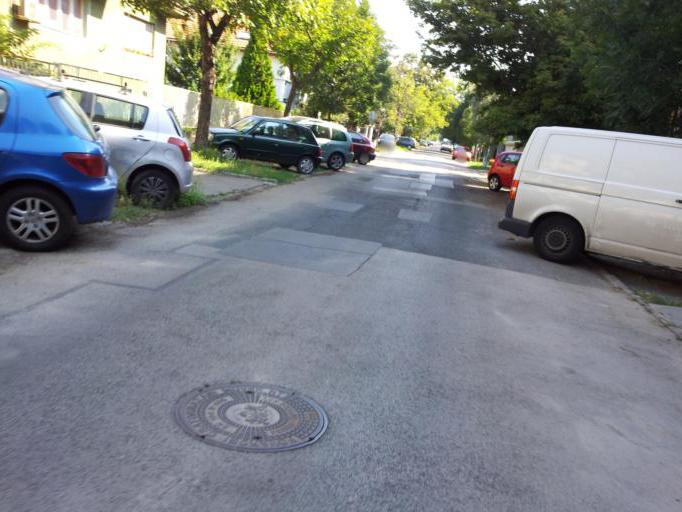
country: HU
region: Budapest
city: Budapest XIV. keruelet
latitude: 47.5136
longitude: 19.1002
